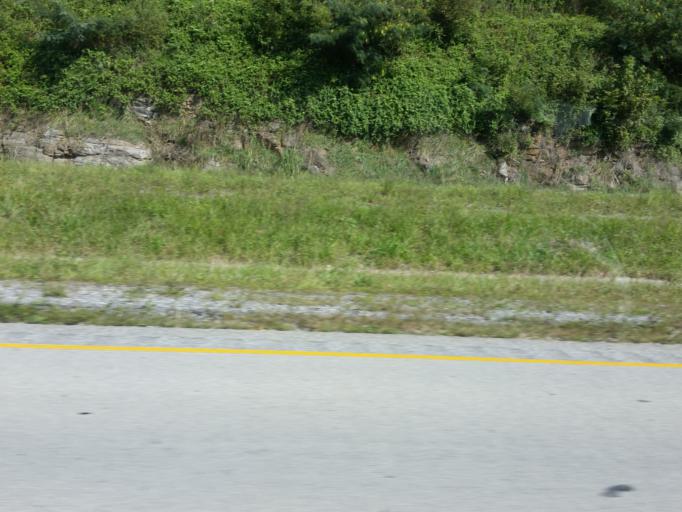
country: US
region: Kentucky
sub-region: Bell County
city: Middlesboro
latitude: 36.6388
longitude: -83.7044
